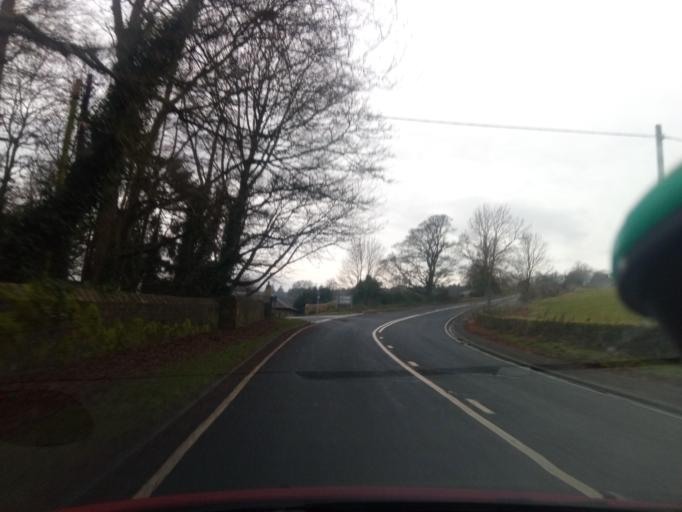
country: GB
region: England
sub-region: Northumberland
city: Wall
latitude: 55.0281
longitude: -2.1469
